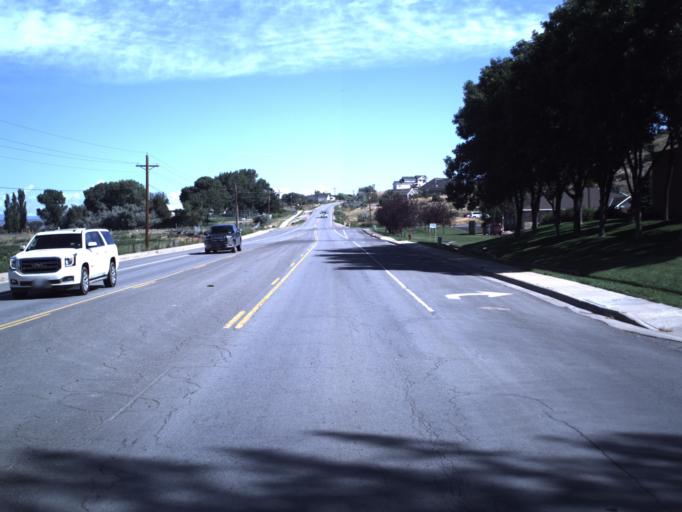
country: US
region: Utah
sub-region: Duchesne County
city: Duchesne
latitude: 40.1713
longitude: -110.4011
